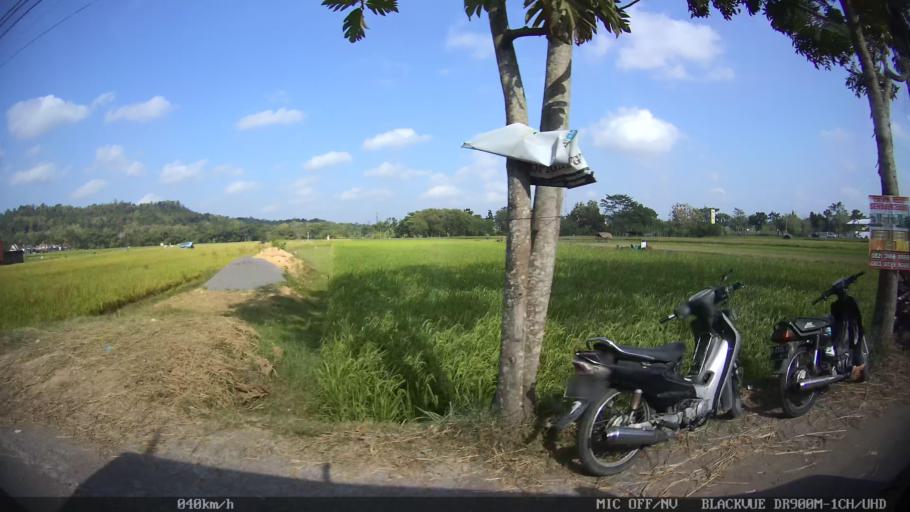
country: ID
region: Daerah Istimewa Yogyakarta
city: Gamping Lor
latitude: -7.8068
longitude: 110.2995
